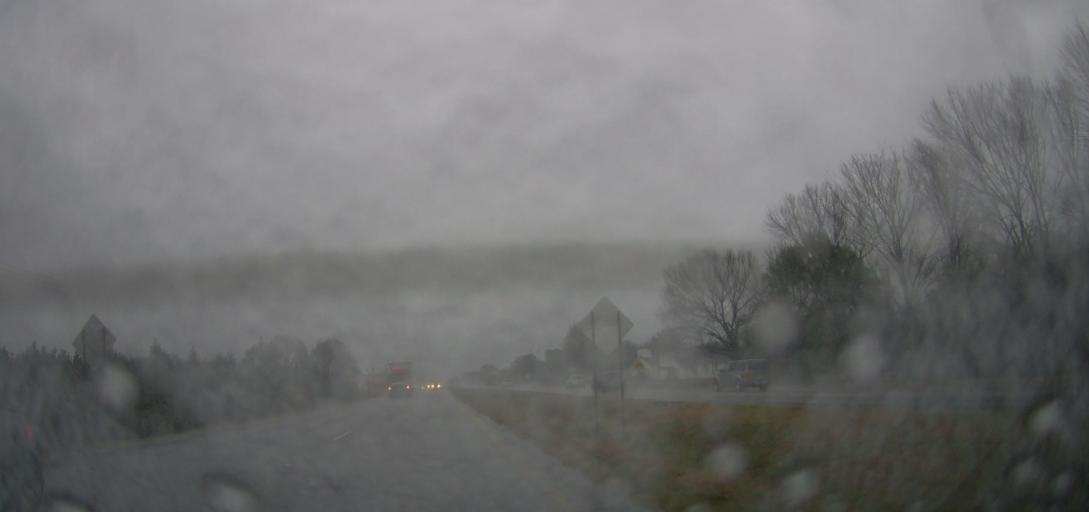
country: US
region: Alabama
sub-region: Elmore County
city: Millbrook
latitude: 32.3957
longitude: -86.3941
